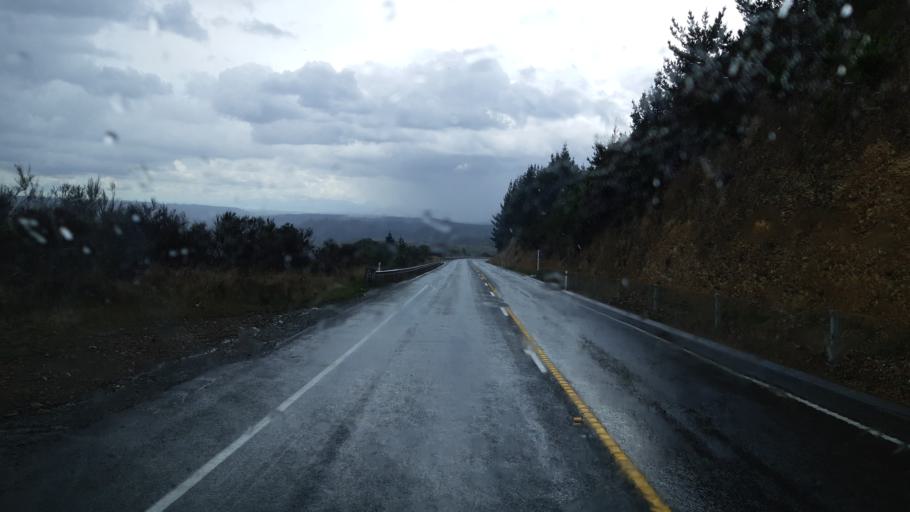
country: NZ
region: Tasman
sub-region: Tasman District
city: Wakefield
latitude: -41.4800
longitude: 172.9166
